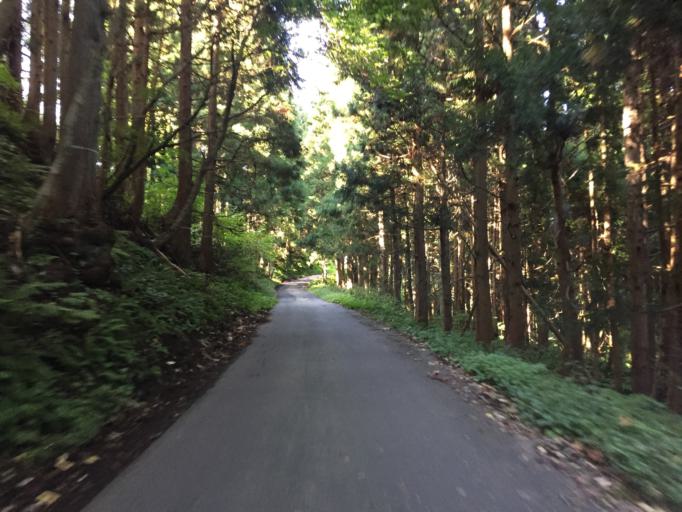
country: JP
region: Yamagata
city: Yonezawa
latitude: 37.8376
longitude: 140.2007
